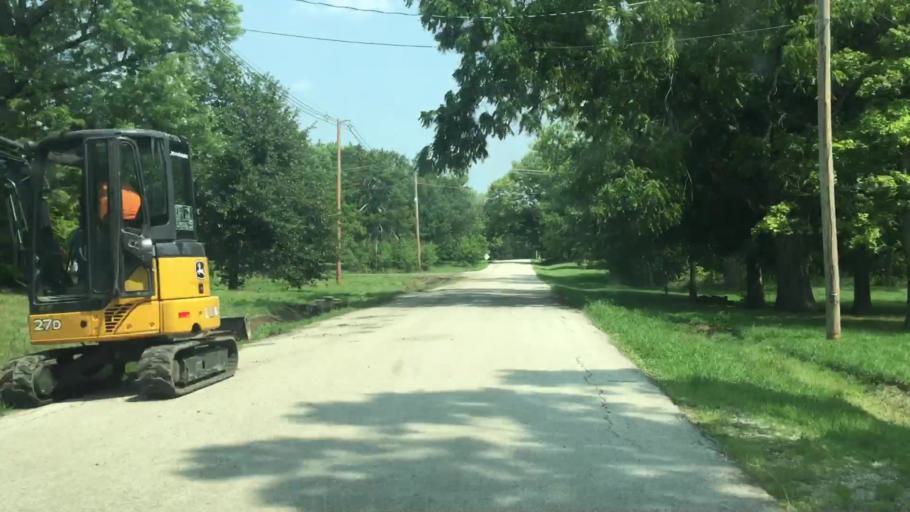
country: US
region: Kansas
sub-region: Douglas County
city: Baldwin City
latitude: 38.7722
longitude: -95.2034
